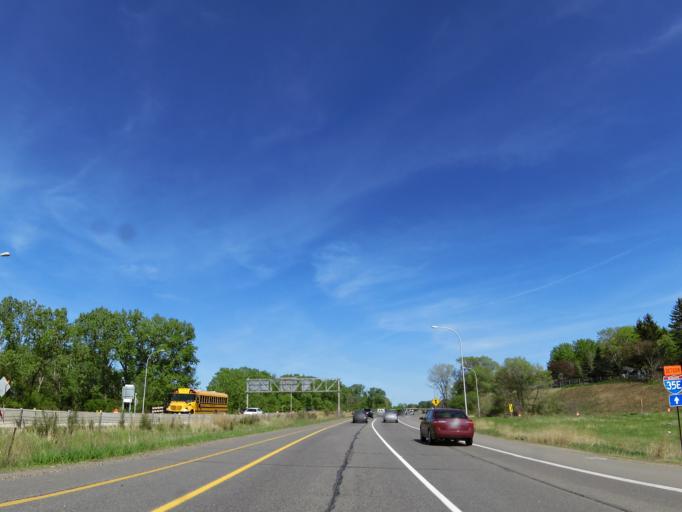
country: US
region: Minnesota
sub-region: Ramsey County
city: Little Canada
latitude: 45.0106
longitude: -93.0876
